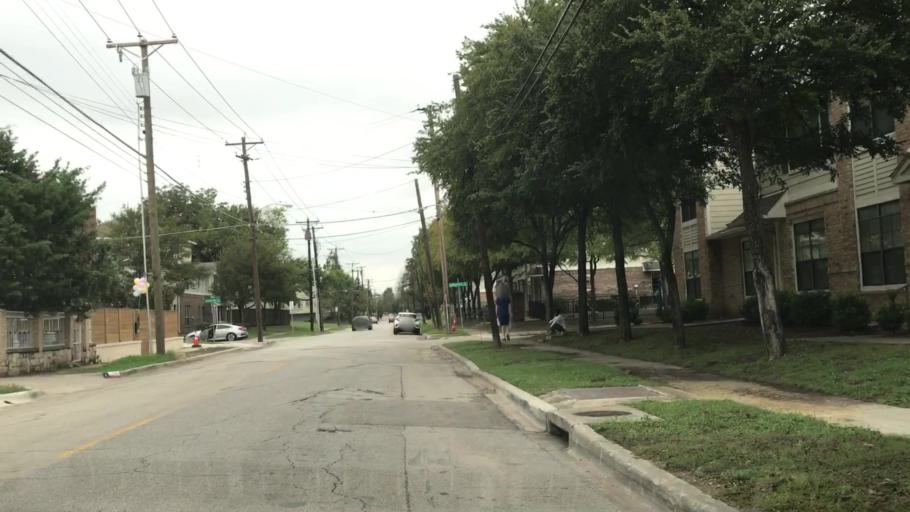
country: US
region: Texas
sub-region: Dallas County
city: Highland Park
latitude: 32.8049
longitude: -96.7828
